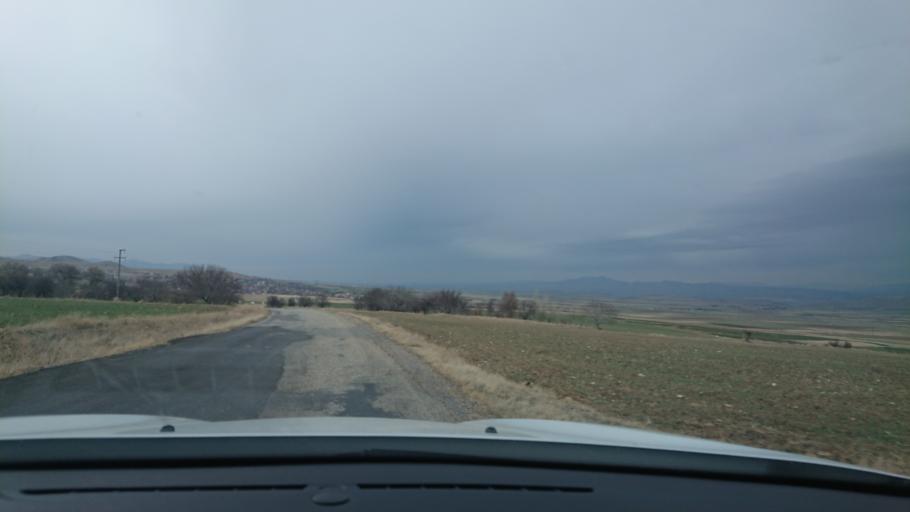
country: TR
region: Aksaray
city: Agacoren
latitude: 38.9461
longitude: 33.9075
